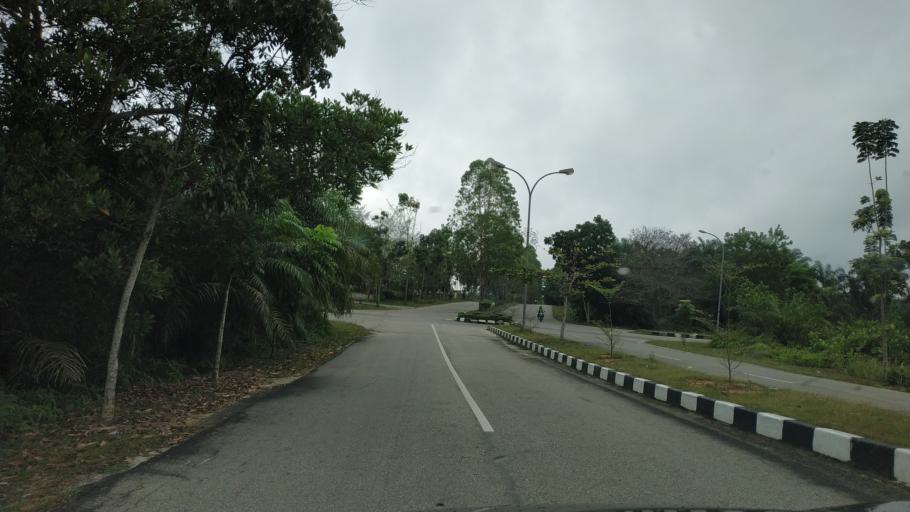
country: ID
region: Riau
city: Pangkalanbunut
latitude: 0.3803
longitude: 101.8287
